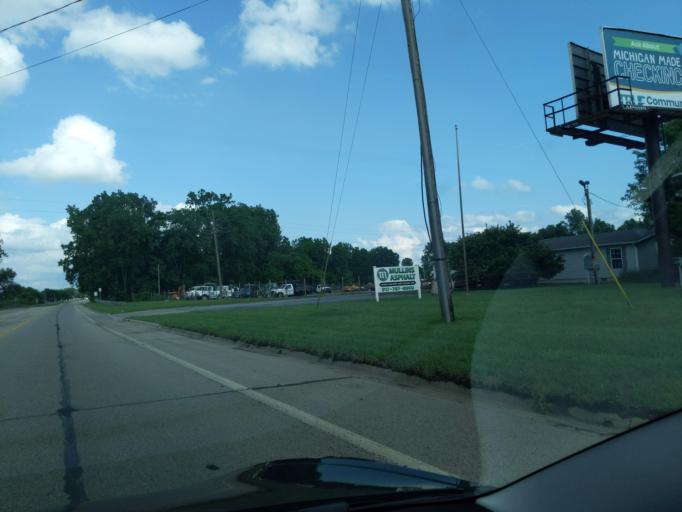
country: US
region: Michigan
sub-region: Jackson County
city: Jackson
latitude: 42.2330
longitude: -84.3906
